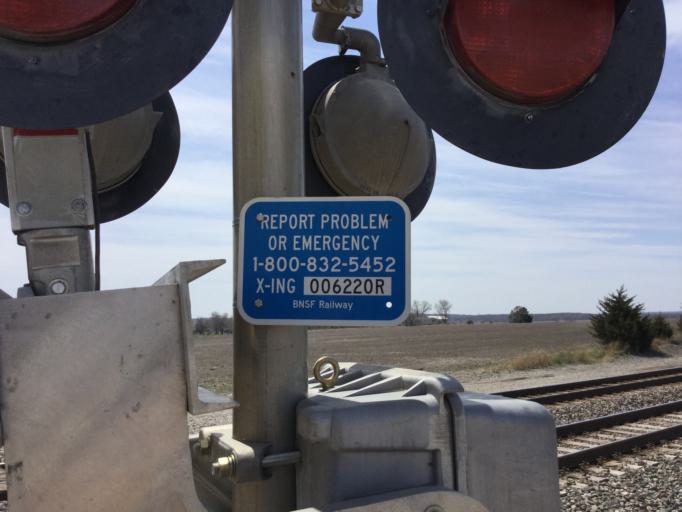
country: US
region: Kansas
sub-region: Franklin County
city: Ottawa
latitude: 38.6154
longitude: -95.3603
